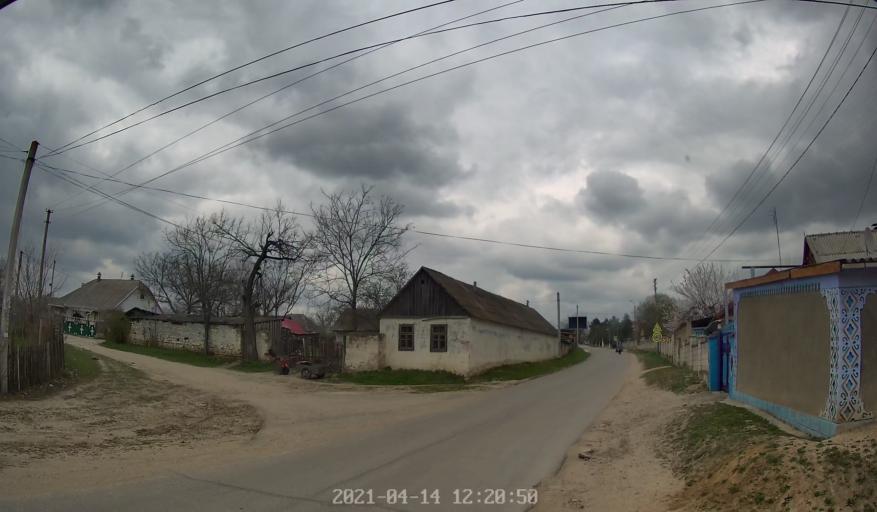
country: MD
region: Criuleni
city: Criuleni
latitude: 47.1672
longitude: 29.1976
